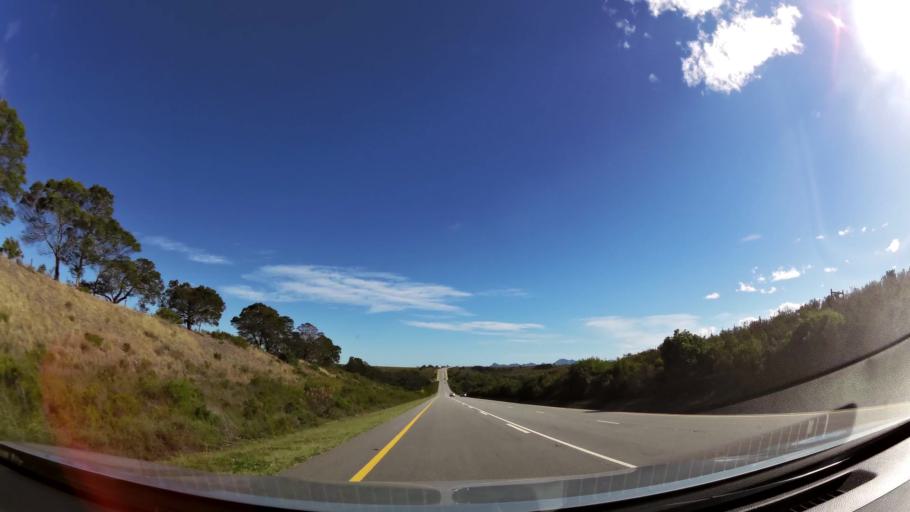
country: ZA
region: Eastern Cape
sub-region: Cacadu District Municipality
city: Kruisfontein
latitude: -34.0060
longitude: 24.6732
